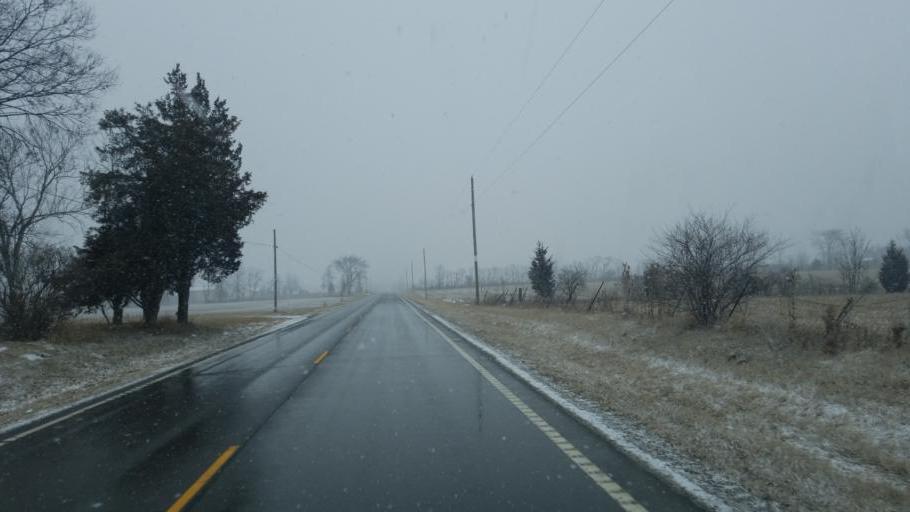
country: US
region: Ohio
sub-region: Defiance County
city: Hicksville
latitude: 41.3441
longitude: -84.7478
